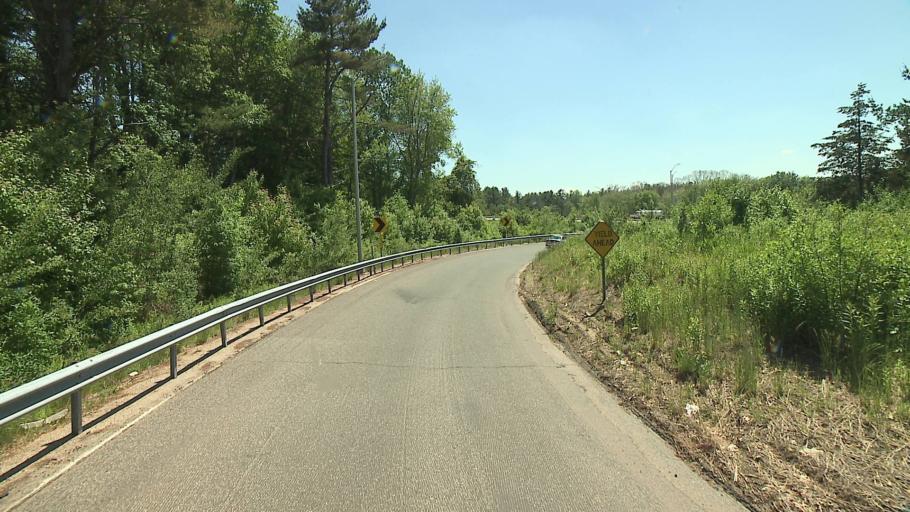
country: US
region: Connecticut
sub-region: Windham County
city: Danielson
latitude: 41.7934
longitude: -71.8747
